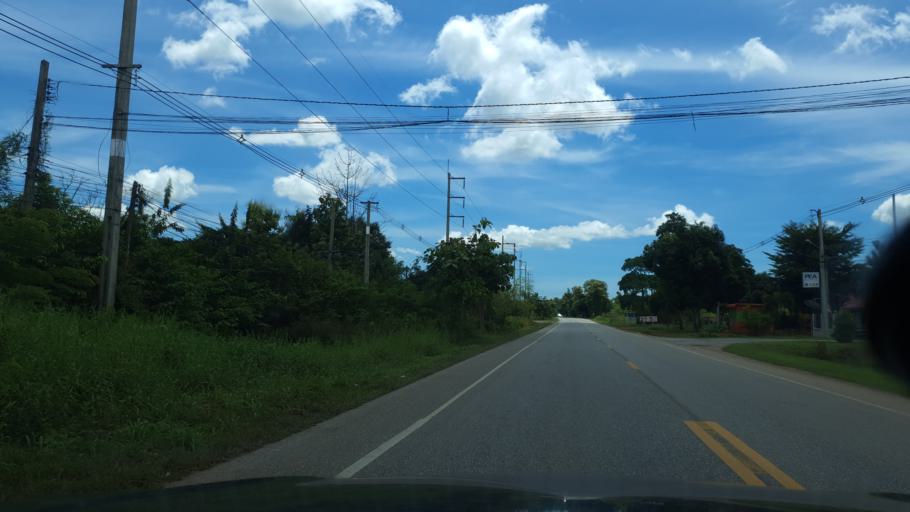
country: TH
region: Sukhothai
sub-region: Amphoe Si Satchanalai
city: Si Satchanalai
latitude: 17.4985
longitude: 99.7585
